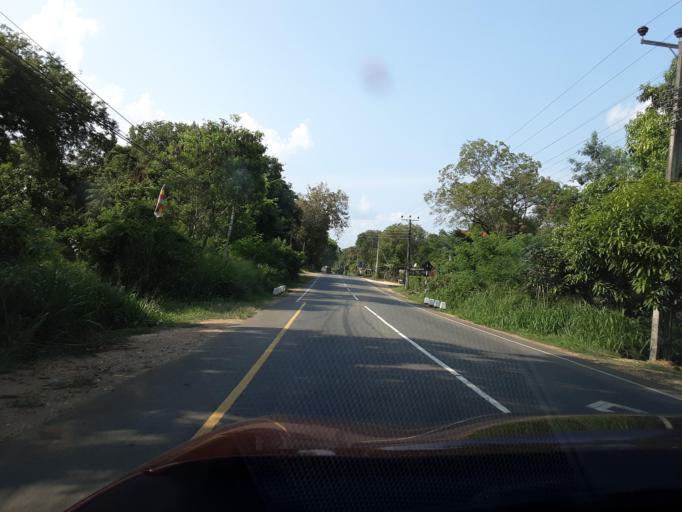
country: LK
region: Uva
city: Haputale
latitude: 6.5910
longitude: 81.1417
